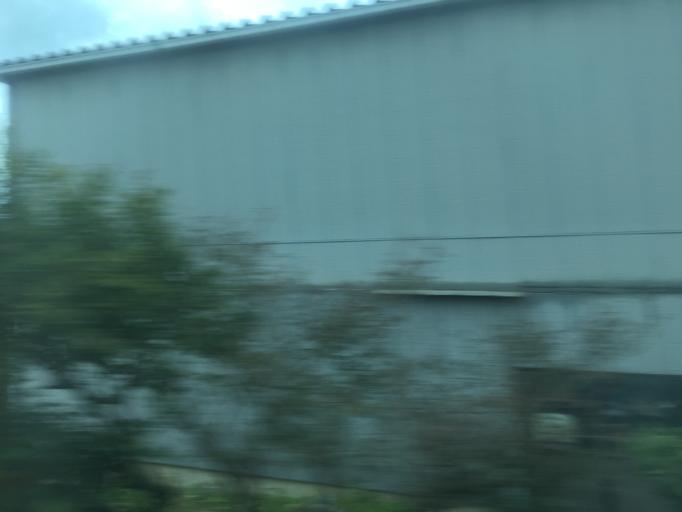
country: JP
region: Niigata
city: Murakami
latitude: 38.2069
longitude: 139.4602
